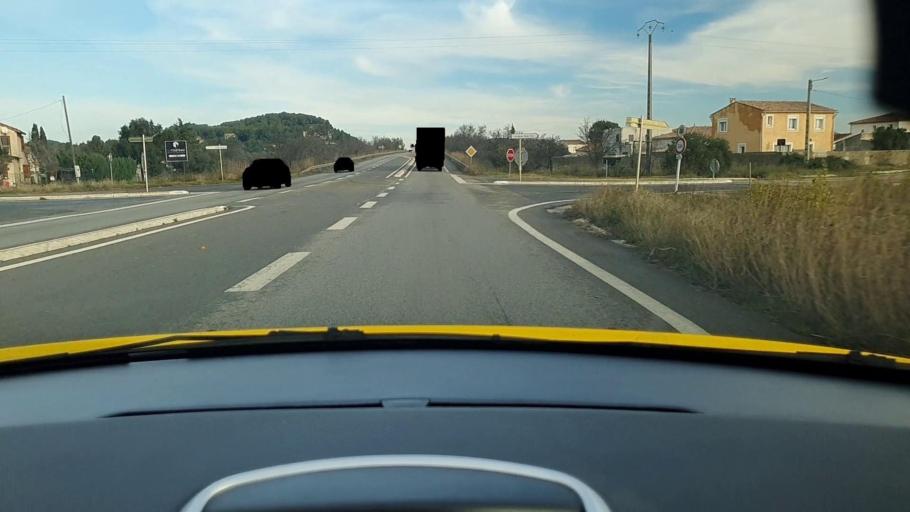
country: FR
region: Languedoc-Roussillon
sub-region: Departement du Gard
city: Beaucaire
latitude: 43.8024
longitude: 4.6083
